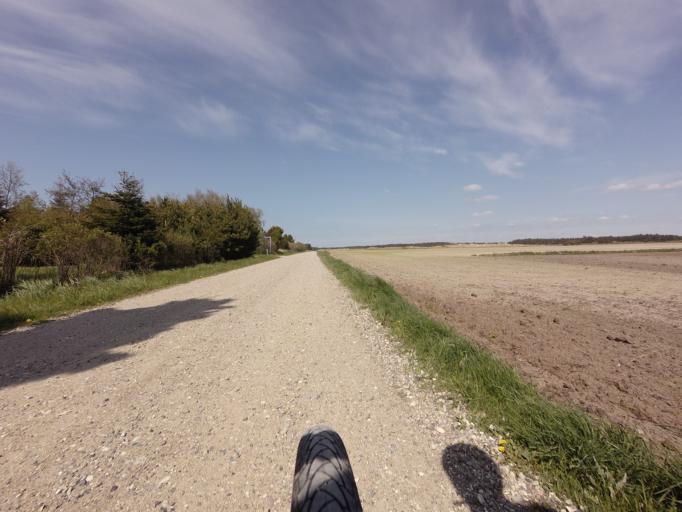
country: DK
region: North Denmark
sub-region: Jammerbugt Kommune
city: Brovst
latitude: 57.2081
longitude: 9.5526
